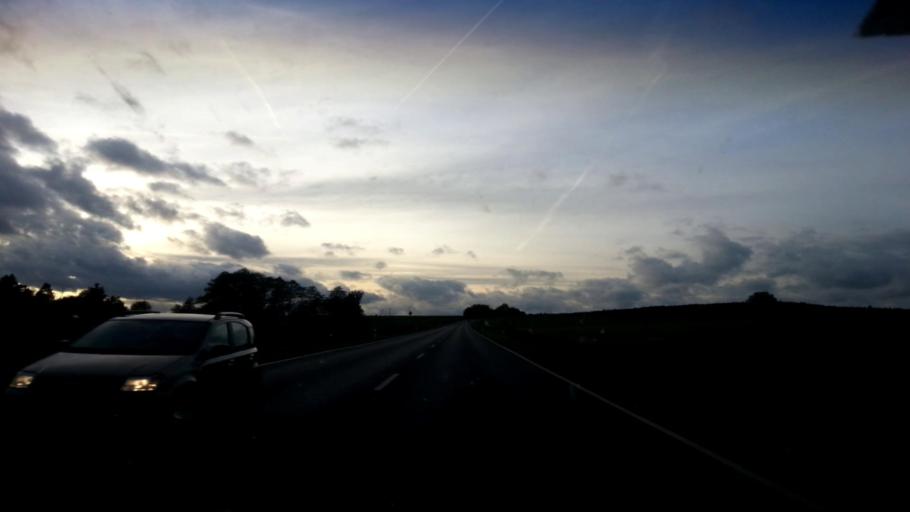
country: DE
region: Bavaria
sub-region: Upper Palatinate
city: Waldsassen
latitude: 50.0049
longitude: 12.2676
